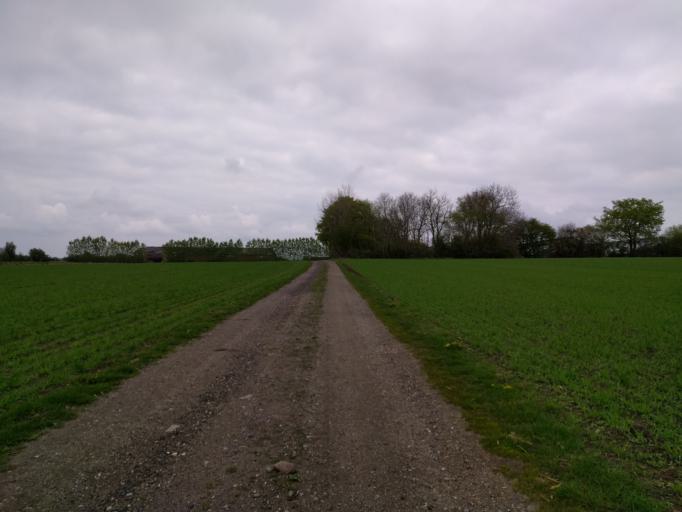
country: DK
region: South Denmark
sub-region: Kerteminde Kommune
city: Langeskov
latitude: 55.4005
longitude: 10.5910
